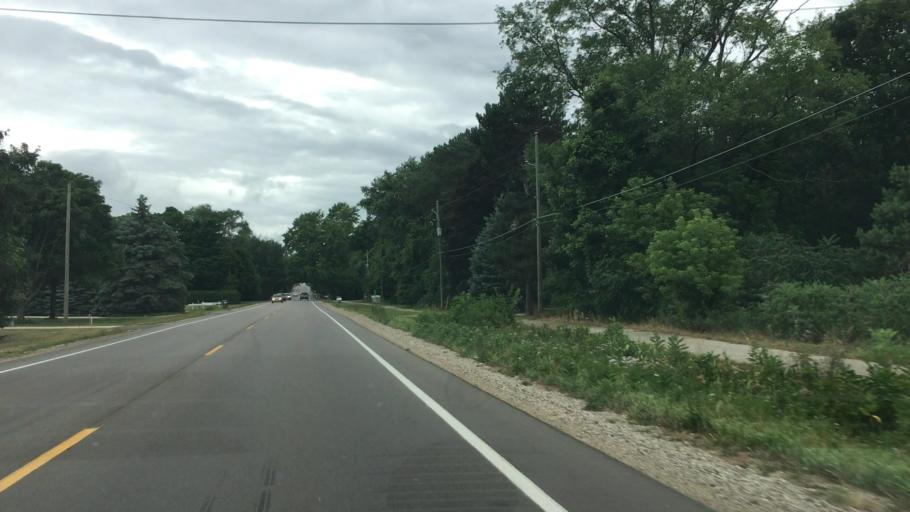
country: US
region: Michigan
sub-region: Ottawa County
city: Zeeland
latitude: 42.7834
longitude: -85.9946
